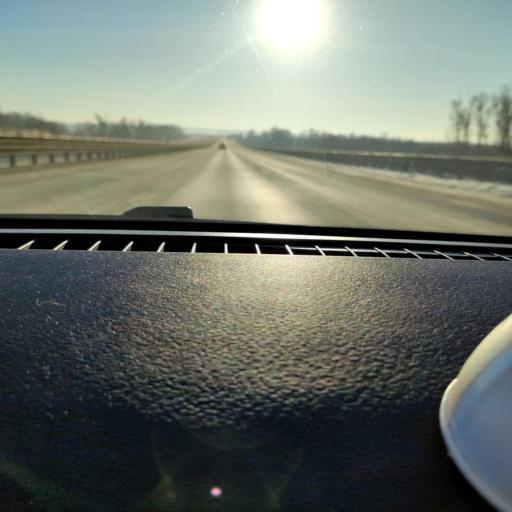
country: RU
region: Samara
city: Smyshlyayevka
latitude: 53.1743
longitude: 50.3110
